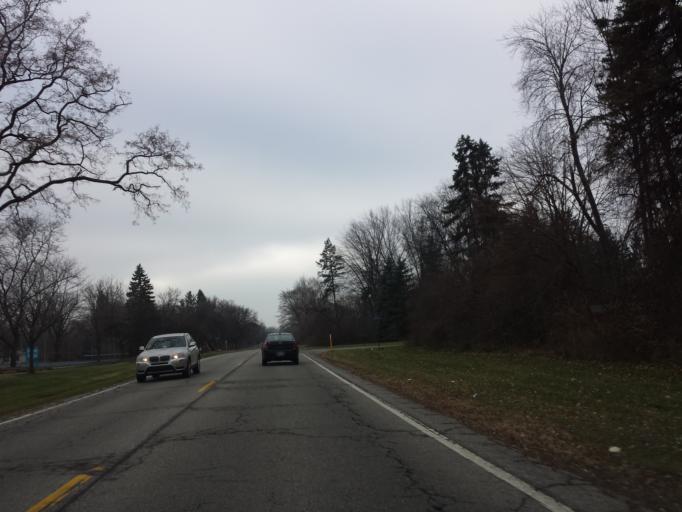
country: US
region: Michigan
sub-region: Oakland County
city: Beverly Hills
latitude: 42.5139
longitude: -83.2425
